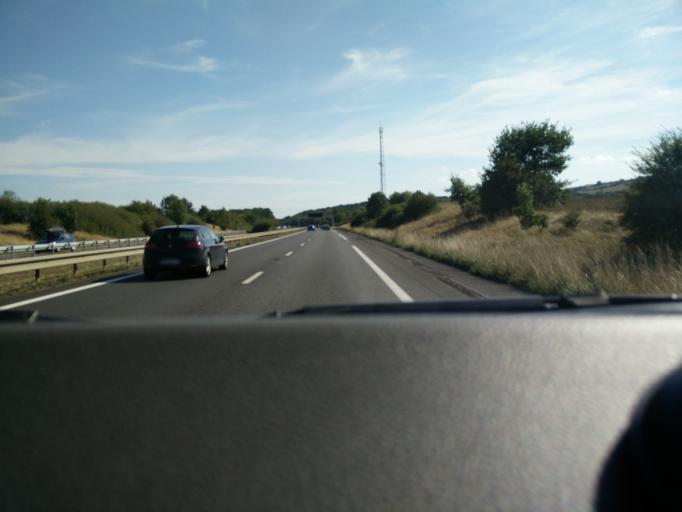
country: FR
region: Lorraine
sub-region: Departement de la Moselle
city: Corny-sur-Moselle
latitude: 48.9794
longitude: 6.1041
